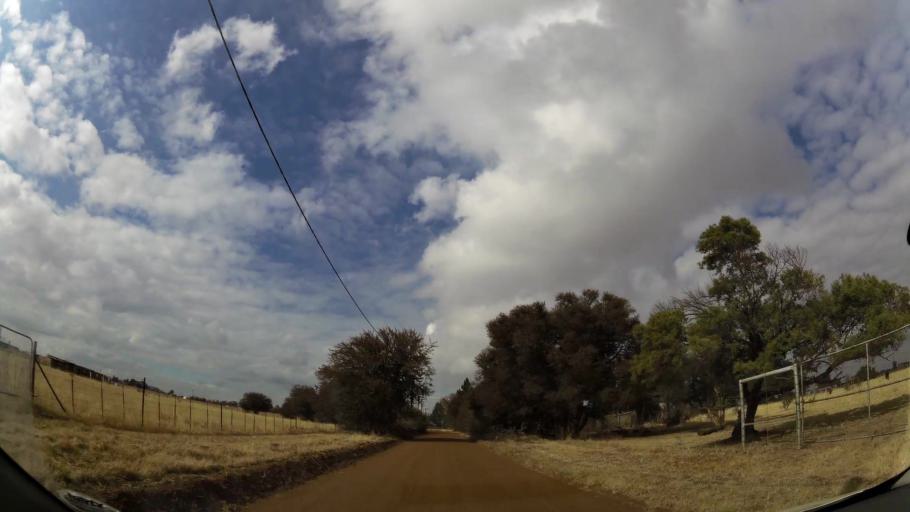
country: ZA
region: Gauteng
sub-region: Sedibeng District Municipality
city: Meyerton
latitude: -26.6137
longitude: 28.0661
